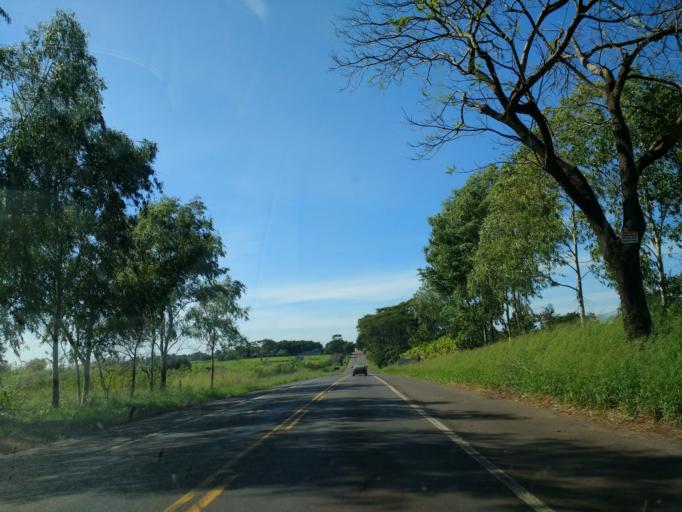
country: BR
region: Parana
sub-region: Alto Piquiri
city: Alto Piquiri
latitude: -23.8917
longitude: -53.4603
